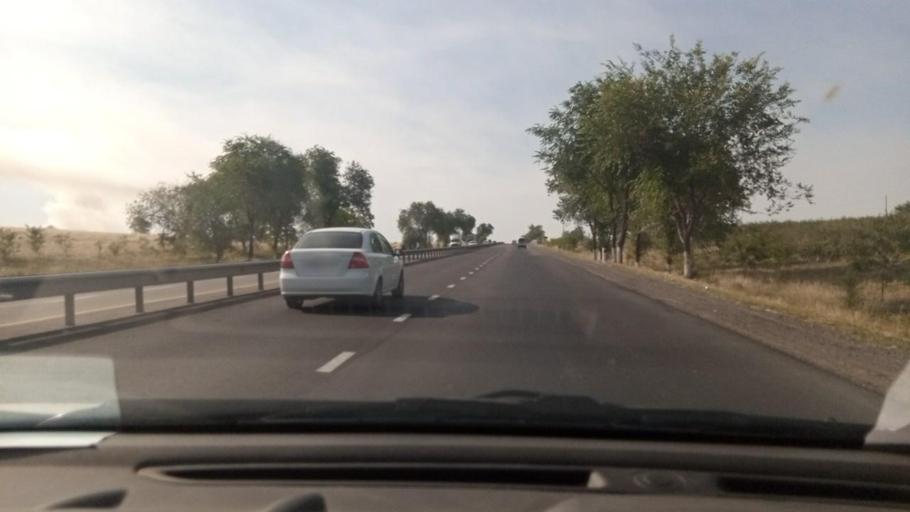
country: UZ
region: Toshkent
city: Tuytepa
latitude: 41.1120
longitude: 69.4478
